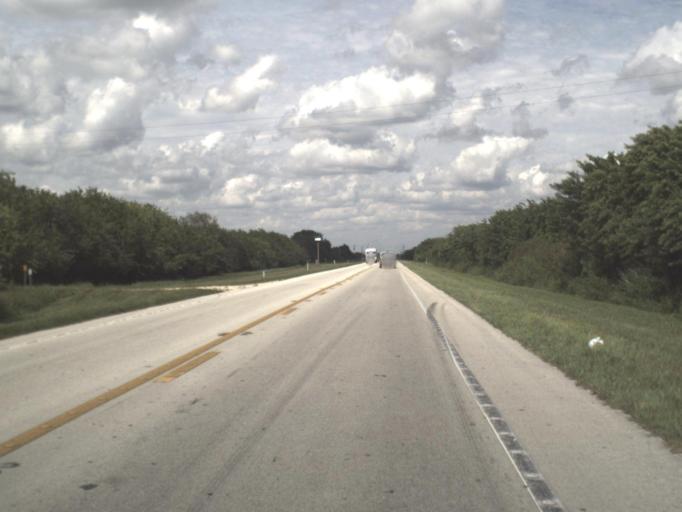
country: US
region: Florida
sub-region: Collier County
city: Immokalee
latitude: 26.4776
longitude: -81.4345
